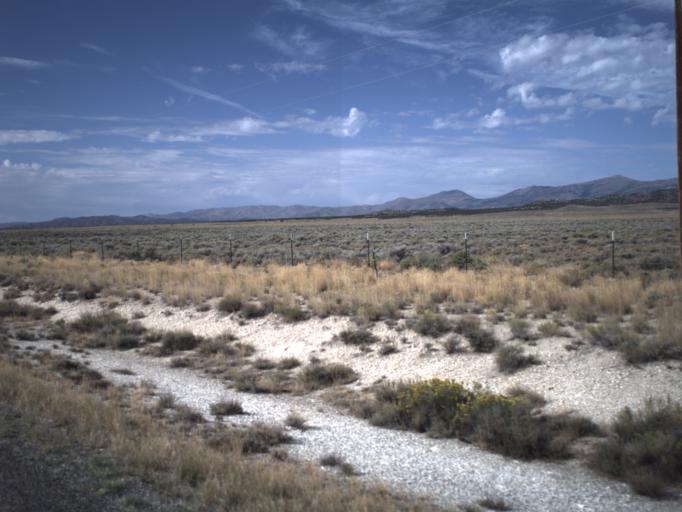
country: US
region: Idaho
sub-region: Cassia County
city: Burley
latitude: 41.7553
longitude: -113.5142
